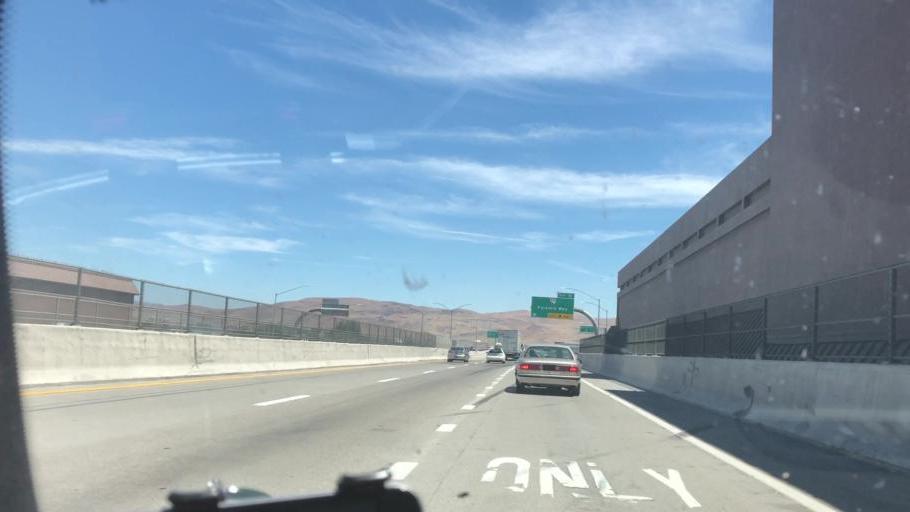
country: US
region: Nevada
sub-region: Washoe County
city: Sparks
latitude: 39.5338
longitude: -119.7582
